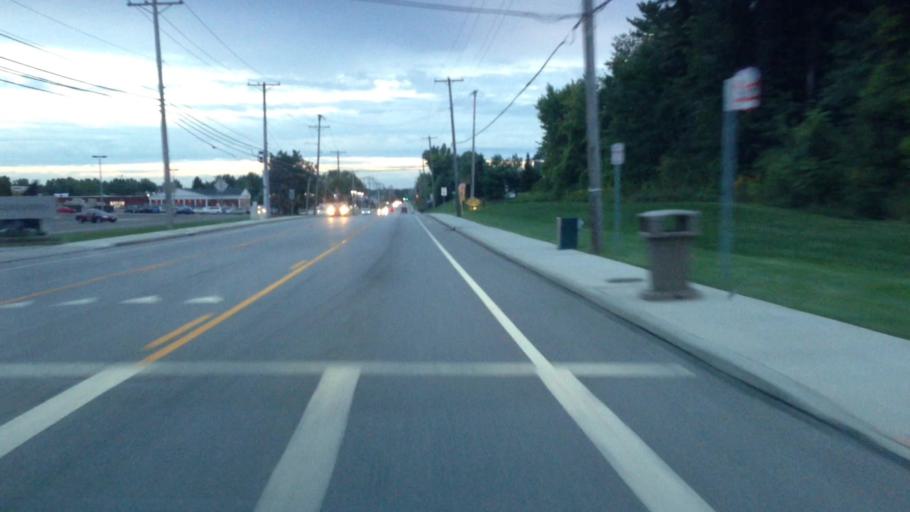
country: US
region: Ohio
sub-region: Summit County
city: Cuyahoga Falls
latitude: 41.1747
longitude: -81.5086
